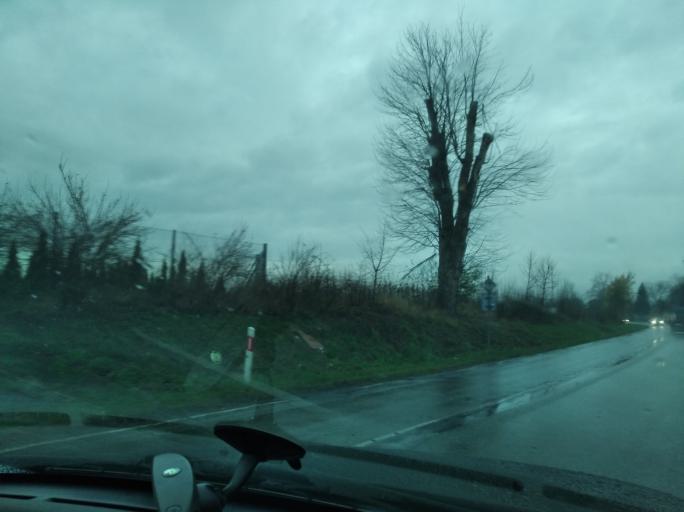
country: PL
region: Subcarpathian Voivodeship
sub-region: Powiat lancucki
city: Albigowa
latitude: 50.0300
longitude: 22.2282
